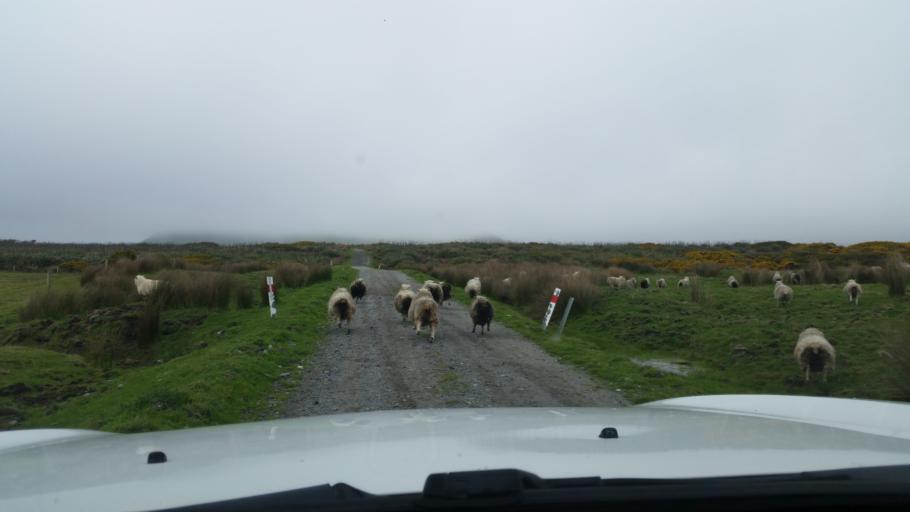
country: NZ
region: Chatham Islands
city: Waitangi
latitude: -43.7859
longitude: -176.8062
